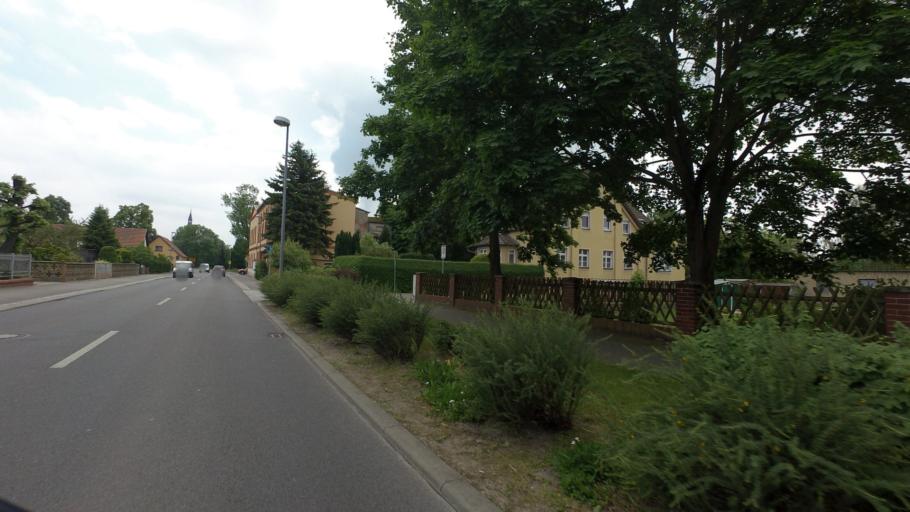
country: DE
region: Brandenburg
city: Peitz
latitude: 51.8598
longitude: 14.4053
